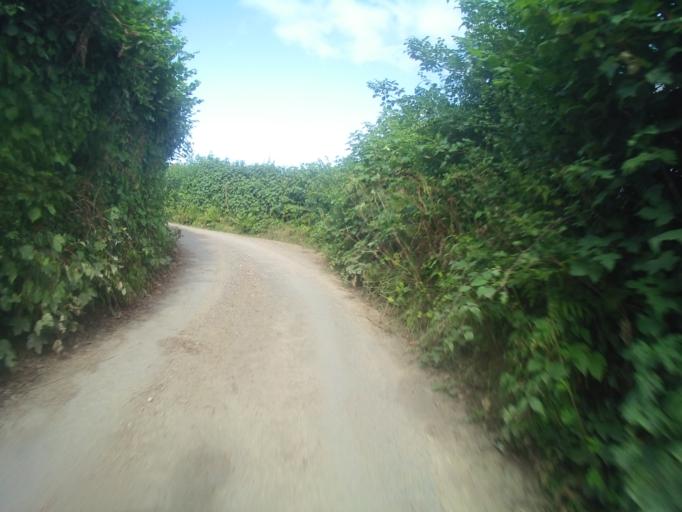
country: GB
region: England
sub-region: Devon
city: Buckfastleigh
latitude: 50.4577
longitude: -3.7474
